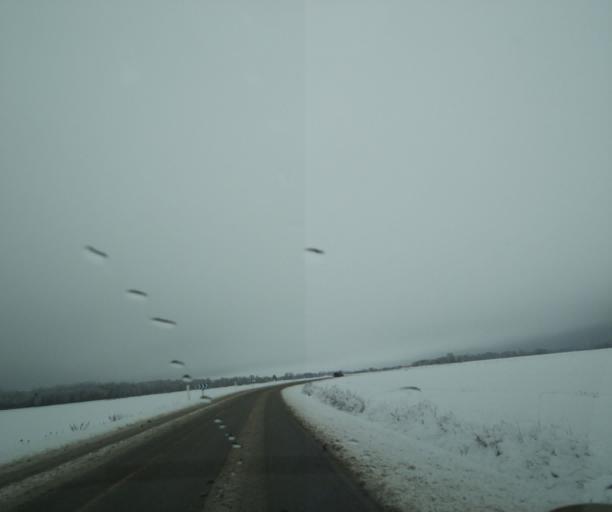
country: FR
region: Champagne-Ardenne
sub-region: Departement de la Haute-Marne
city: Wassy
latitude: 48.5325
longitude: 4.9248
